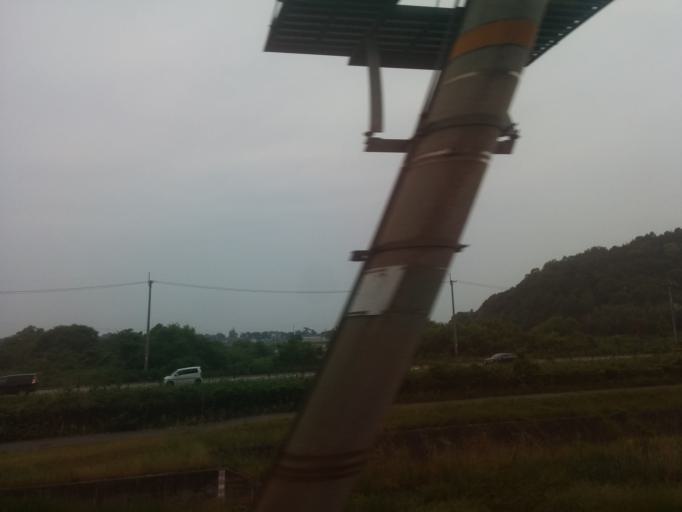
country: JP
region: Shiga Prefecture
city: Hikone
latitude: 35.2923
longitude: 136.2648
